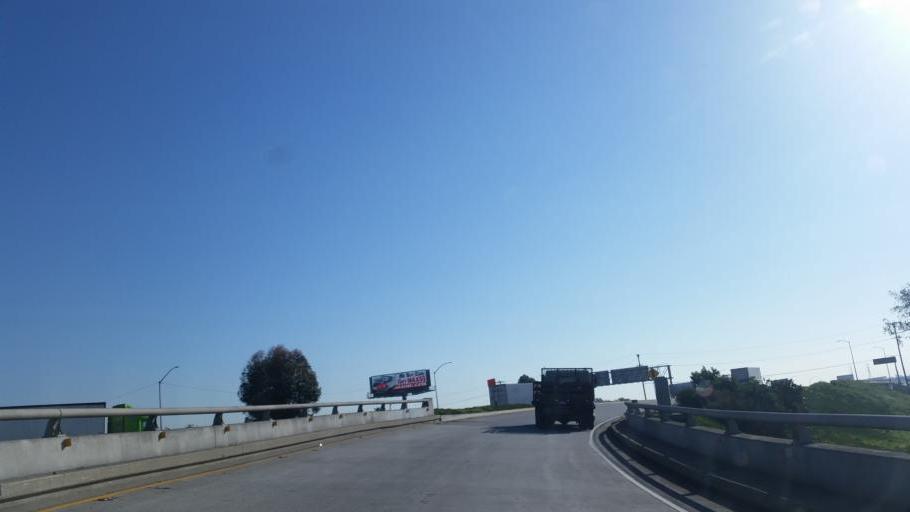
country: US
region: California
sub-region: Los Angeles County
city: Carson
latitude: 33.8542
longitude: -118.2825
